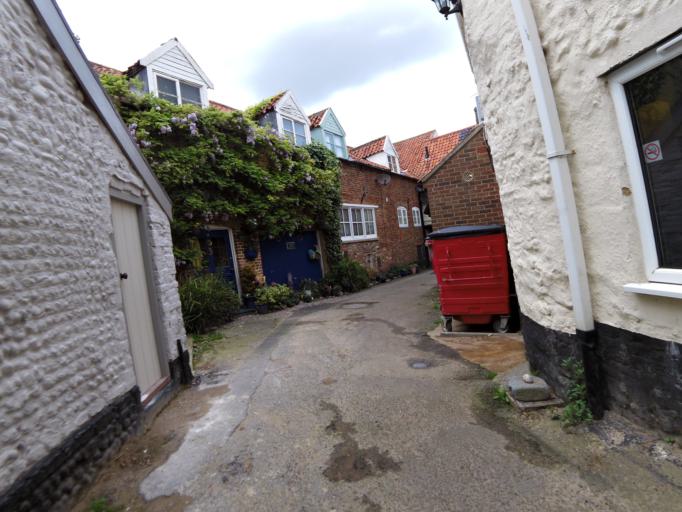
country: GB
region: England
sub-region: Norfolk
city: Wells-next-the-Sea
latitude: 52.9570
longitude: 0.8515
